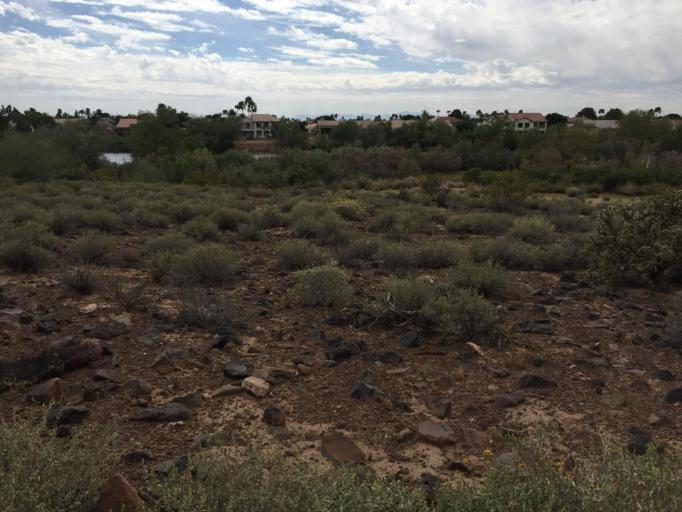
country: US
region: Arizona
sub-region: Maricopa County
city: Peoria
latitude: 33.6852
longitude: -112.1833
